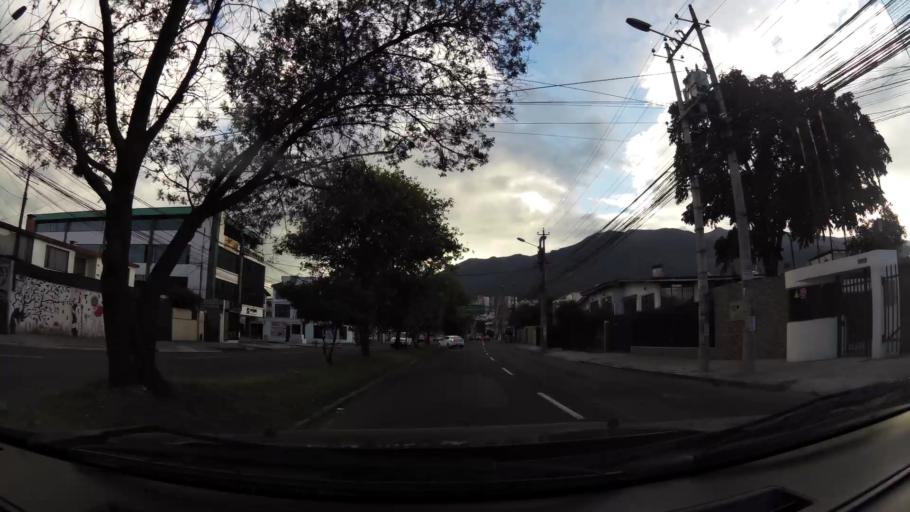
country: EC
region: Pichincha
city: Quito
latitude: -0.1581
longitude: -78.4822
